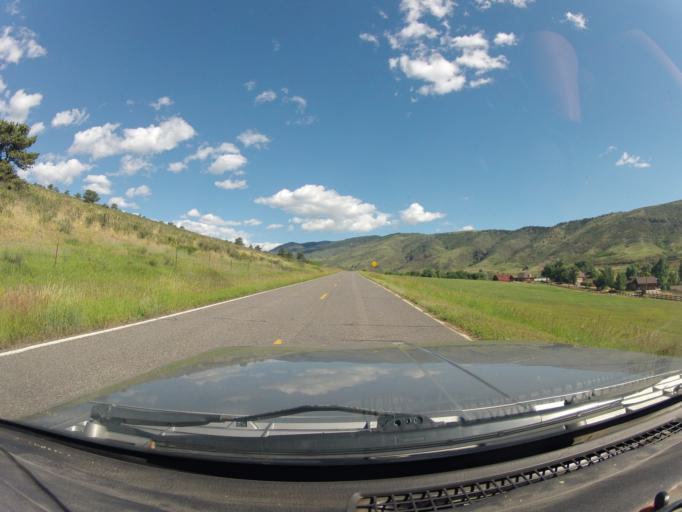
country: US
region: Colorado
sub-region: Larimer County
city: Laporte
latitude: 40.4956
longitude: -105.2230
